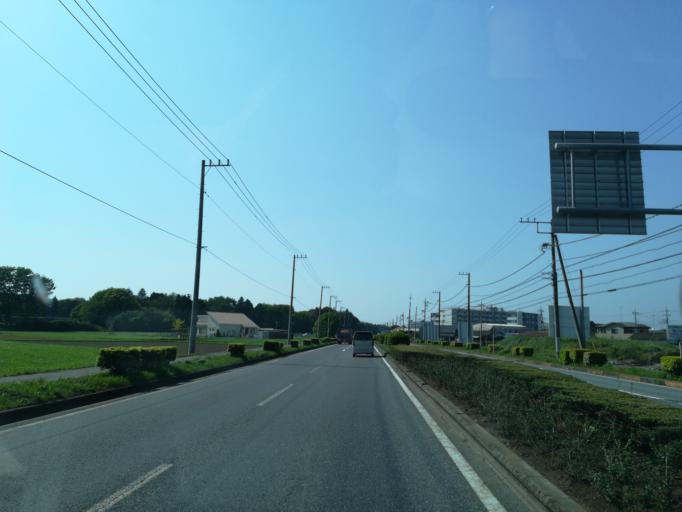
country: JP
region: Ibaraki
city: Tsukuba
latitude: 36.1042
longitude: 140.0833
